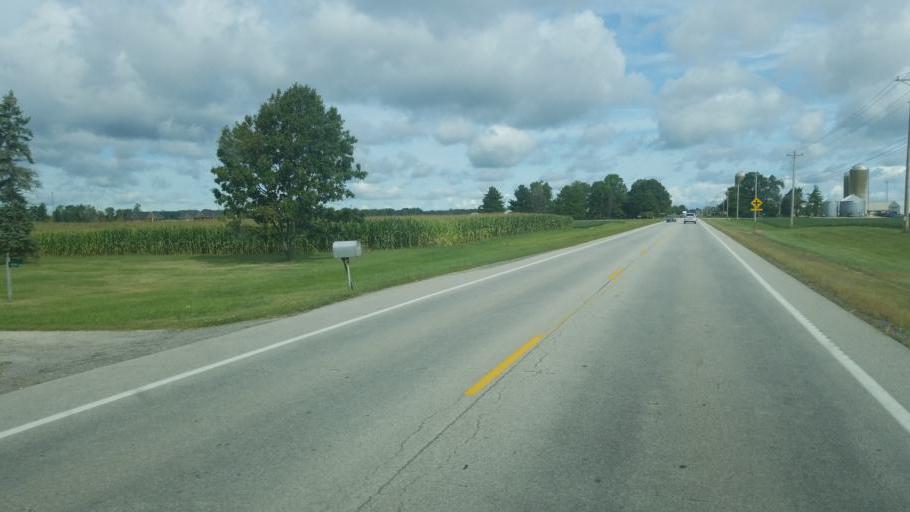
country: US
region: Ohio
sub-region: Lorain County
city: Oberlin
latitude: 41.2479
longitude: -82.2178
